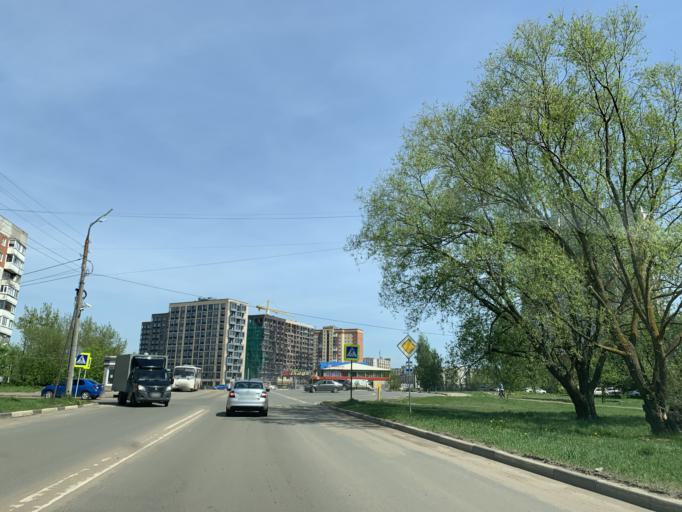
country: RU
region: Jaroslavl
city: Yaroslavl
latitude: 57.6530
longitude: 39.9610
